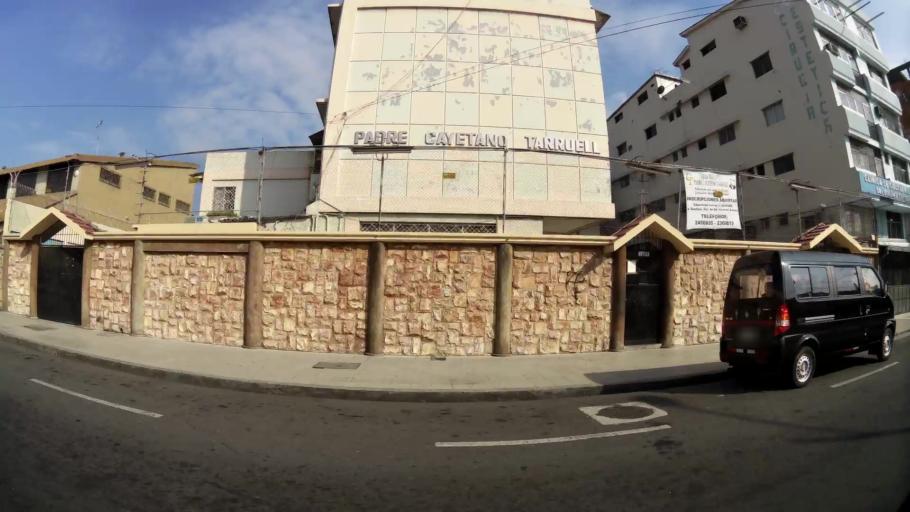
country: EC
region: Guayas
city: Guayaquil
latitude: -2.1919
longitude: -79.8969
